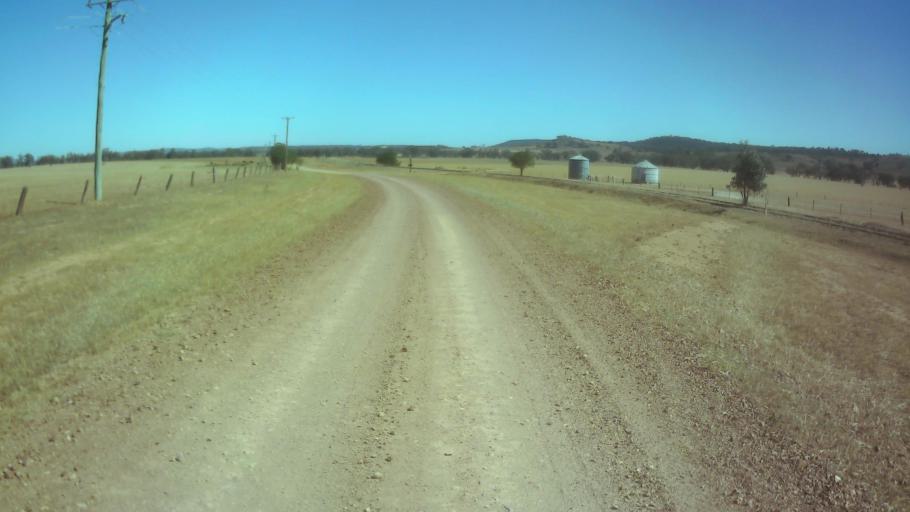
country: AU
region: New South Wales
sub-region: Weddin
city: Grenfell
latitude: -33.9541
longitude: 148.3017
